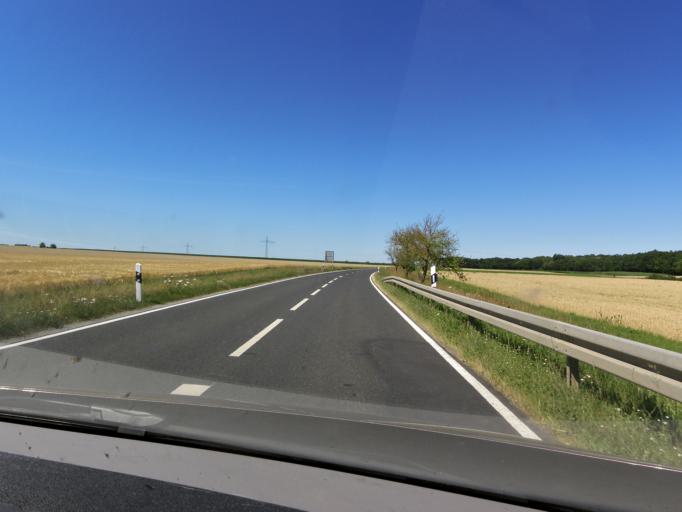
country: DE
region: Bavaria
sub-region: Regierungsbezirk Unterfranken
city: Frickenhausen
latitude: 49.7126
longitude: 10.0802
